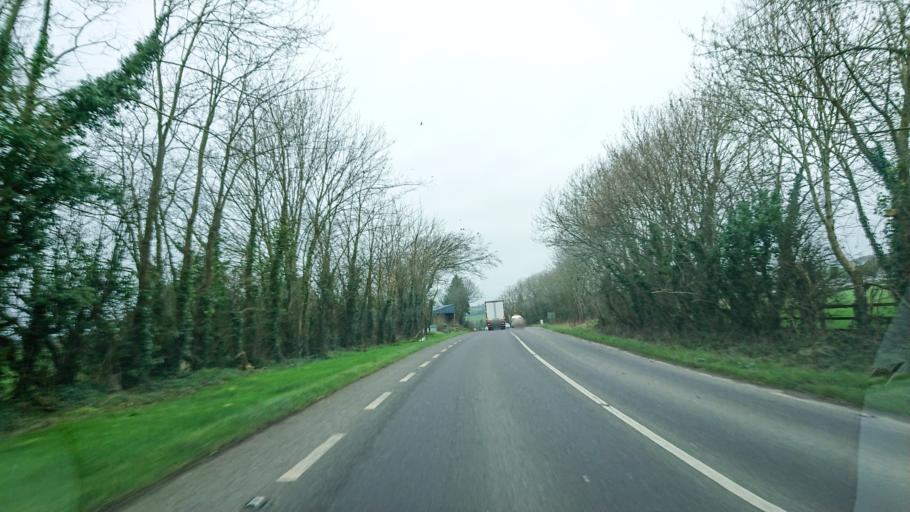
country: IE
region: Munster
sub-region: County Cork
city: Bandon
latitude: 51.7431
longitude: -8.8159
